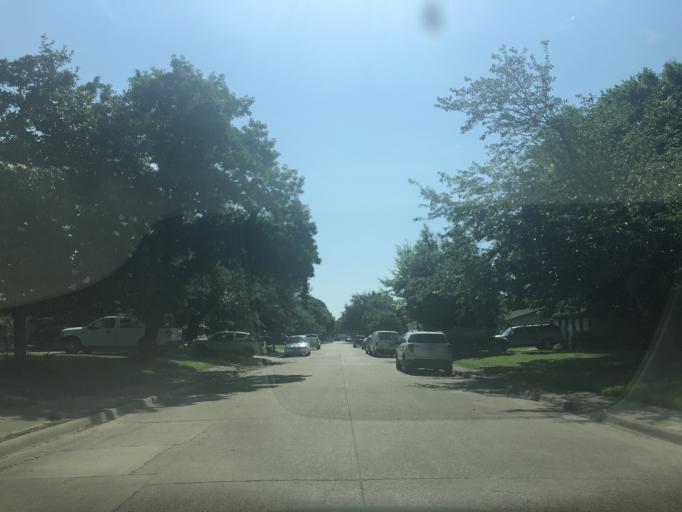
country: US
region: Texas
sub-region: Dallas County
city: Grand Prairie
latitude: 32.7181
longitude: -97.0006
